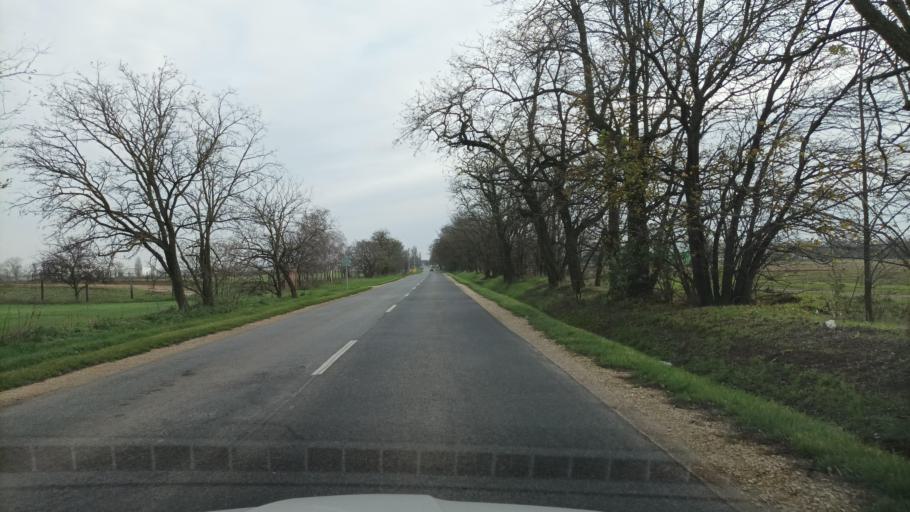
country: HU
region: Pest
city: Ocsa
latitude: 47.3102
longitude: 19.2096
